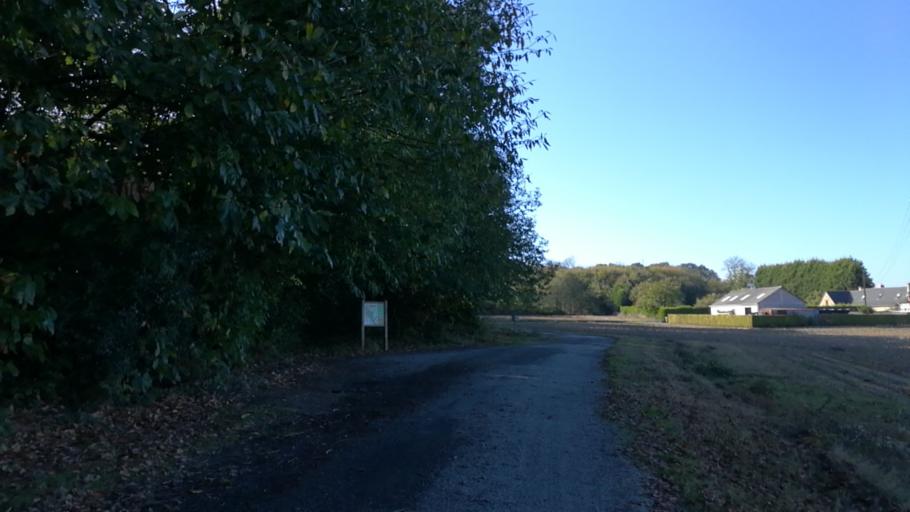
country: FR
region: Brittany
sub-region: Departement d'Ille-et-Vilaine
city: Retiers
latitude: 47.9128
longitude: -1.3985
